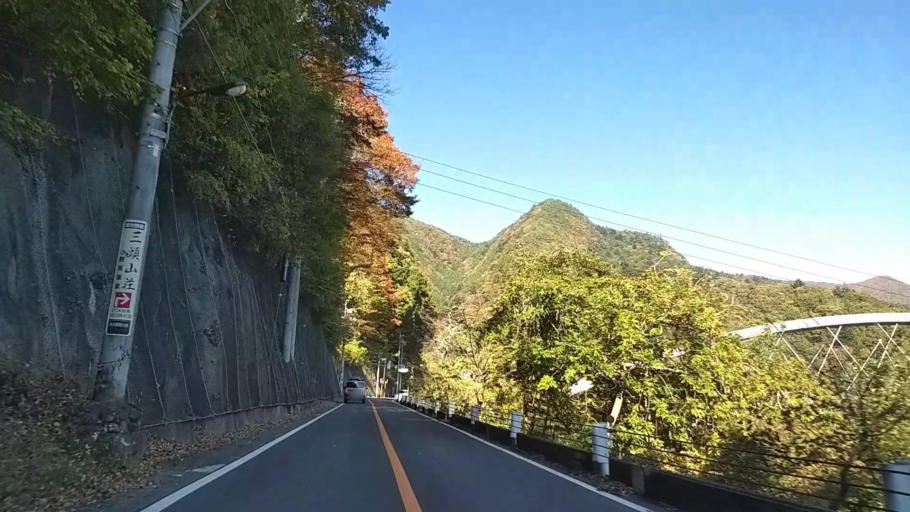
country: JP
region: Yamanashi
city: Otsuki
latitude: 35.7722
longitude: 138.9972
